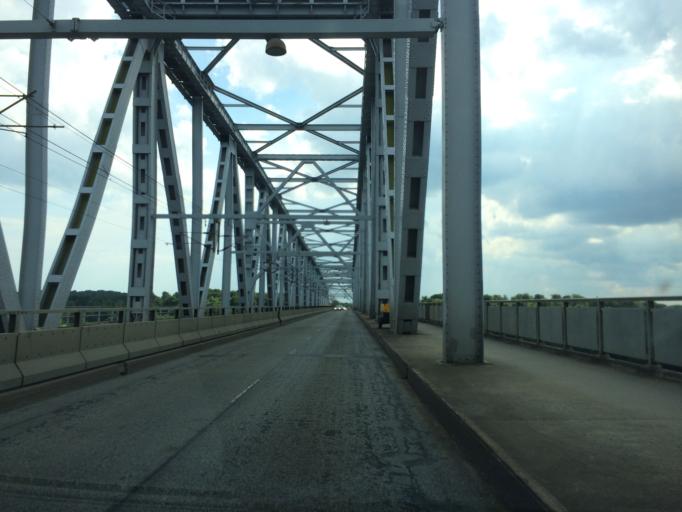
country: DK
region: South Denmark
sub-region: Fredericia Kommune
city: Snoghoj
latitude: 55.5177
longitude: 9.7098
